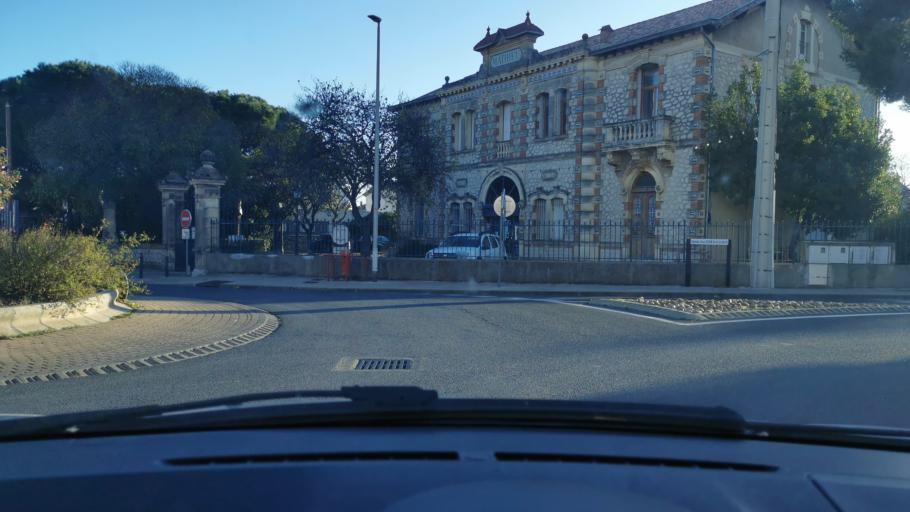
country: FR
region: Languedoc-Roussillon
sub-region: Departement de l'Herault
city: Frontignan
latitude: 43.4490
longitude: 3.7511
